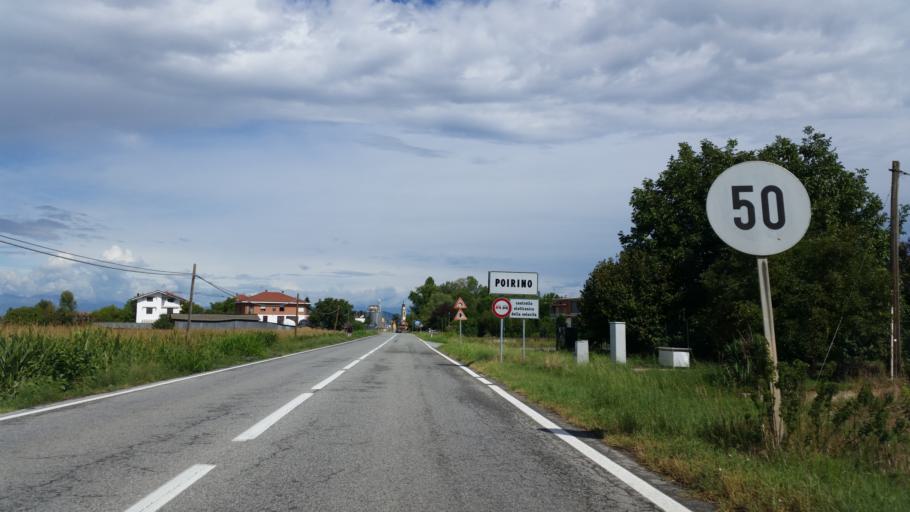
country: IT
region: Piedmont
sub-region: Provincia di Torino
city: Poirino
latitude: 44.9103
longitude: 7.8517
